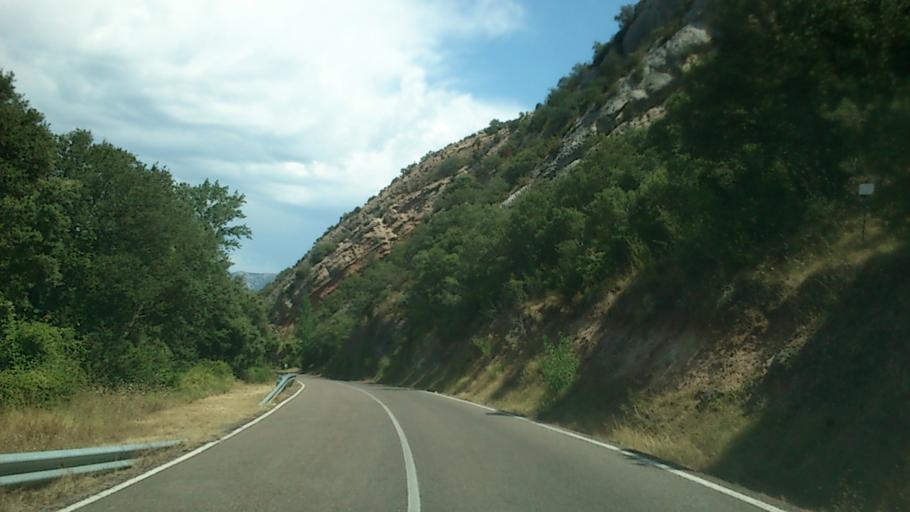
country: ES
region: Castille and Leon
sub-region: Provincia de Burgos
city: Frias
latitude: 42.7605
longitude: -3.2676
